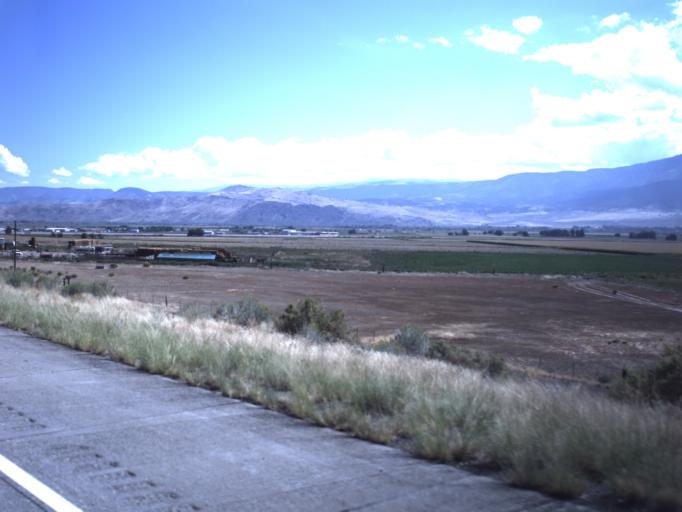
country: US
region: Utah
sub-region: Sevier County
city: Richfield
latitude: 38.7296
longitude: -112.1248
